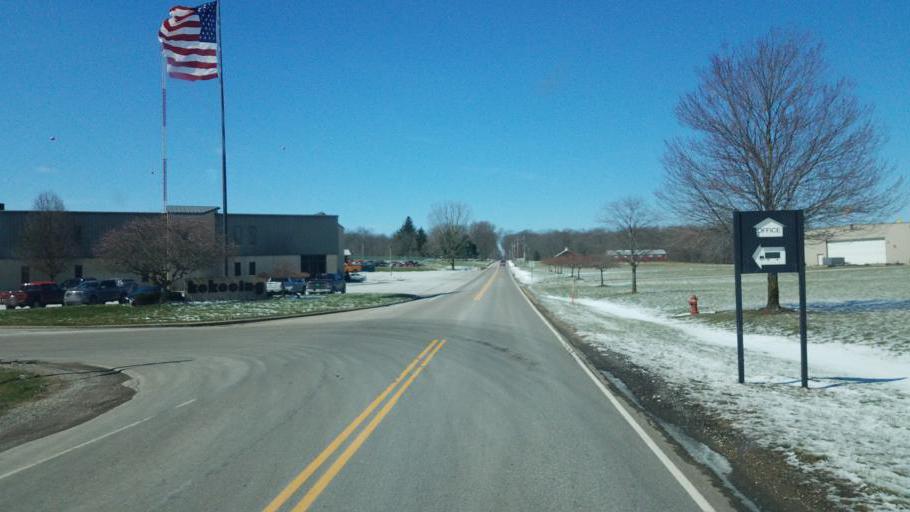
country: US
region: Ohio
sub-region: Knox County
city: Fredericktown
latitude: 40.4919
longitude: -82.5591
